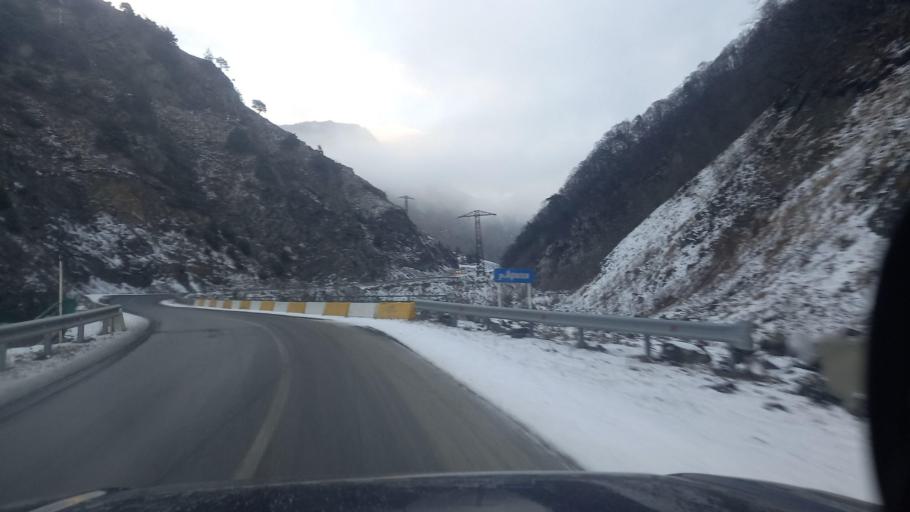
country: RU
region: Ingushetiya
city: Dzhayrakh
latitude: 42.7904
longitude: 44.7720
